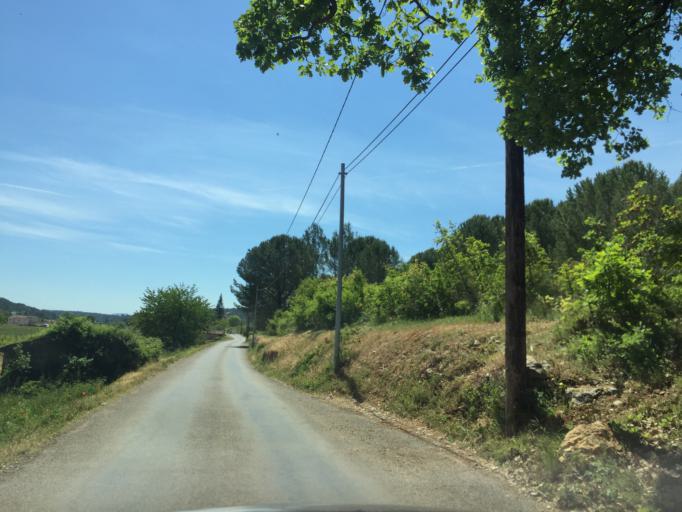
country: FR
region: Provence-Alpes-Cote d'Azur
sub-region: Departement du Var
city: Lorgues
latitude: 43.4830
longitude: 6.3647
